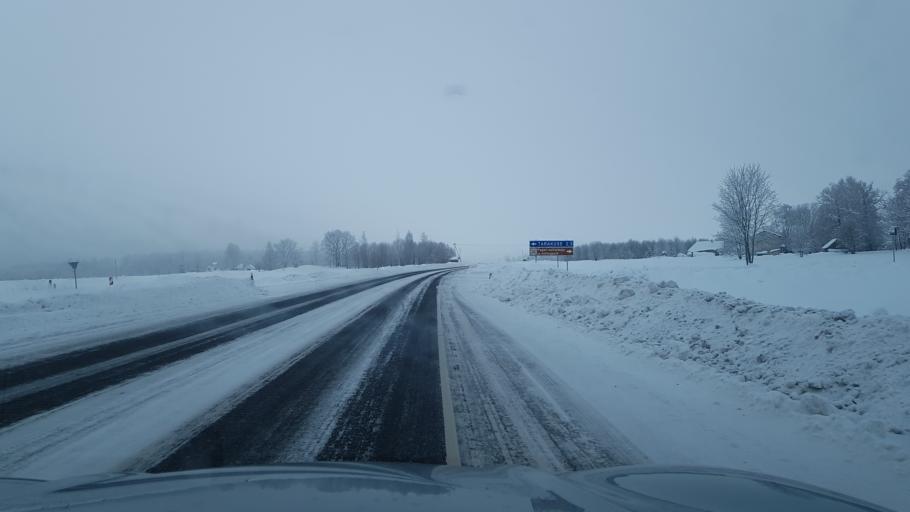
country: EE
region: Ida-Virumaa
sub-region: Johvi vald
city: Johvi
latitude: 59.2596
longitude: 27.3835
